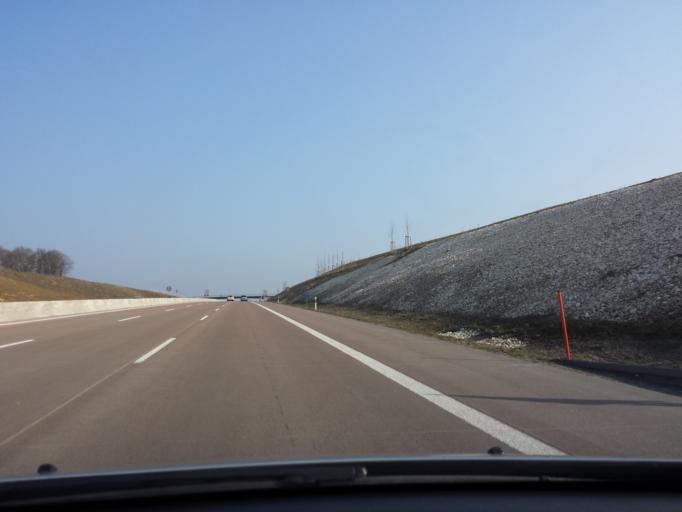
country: DE
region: Bavaria
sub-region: Swabia
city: Burgau
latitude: 48.4252
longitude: 10.3848
